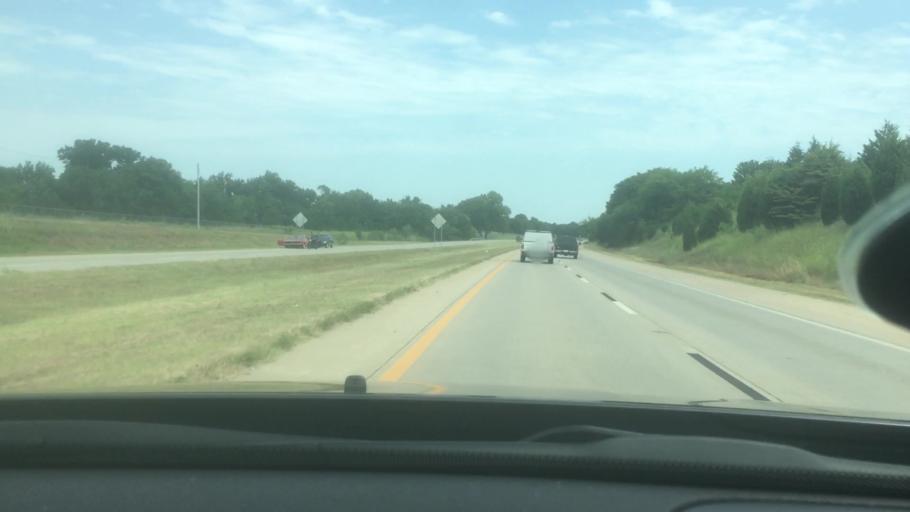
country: US
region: Oklahoma
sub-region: Pottawatomie County
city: Tecumseh
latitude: 35.2909
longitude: -96.9423
